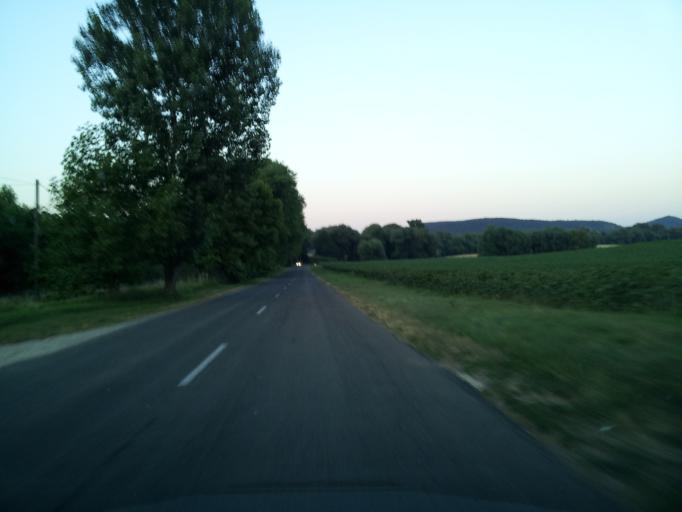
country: HU
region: Fejer
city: Szarliget
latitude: 47.5248
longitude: 18.4750
